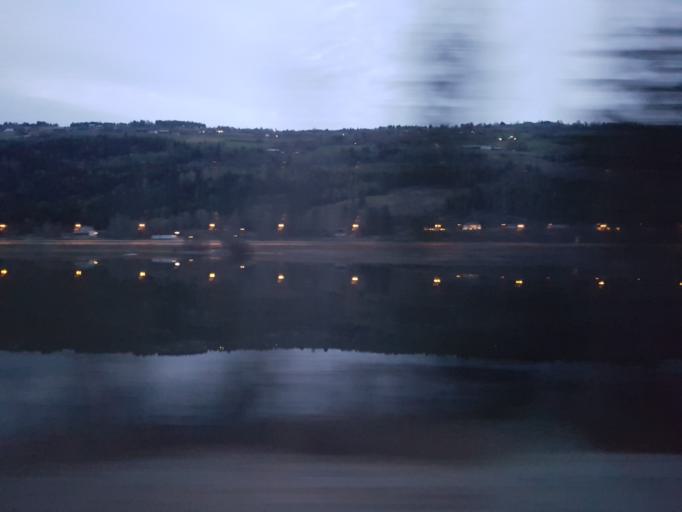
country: NO
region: Oppland
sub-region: Oyer
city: Tretten
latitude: 61.2677
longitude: 10.3992
